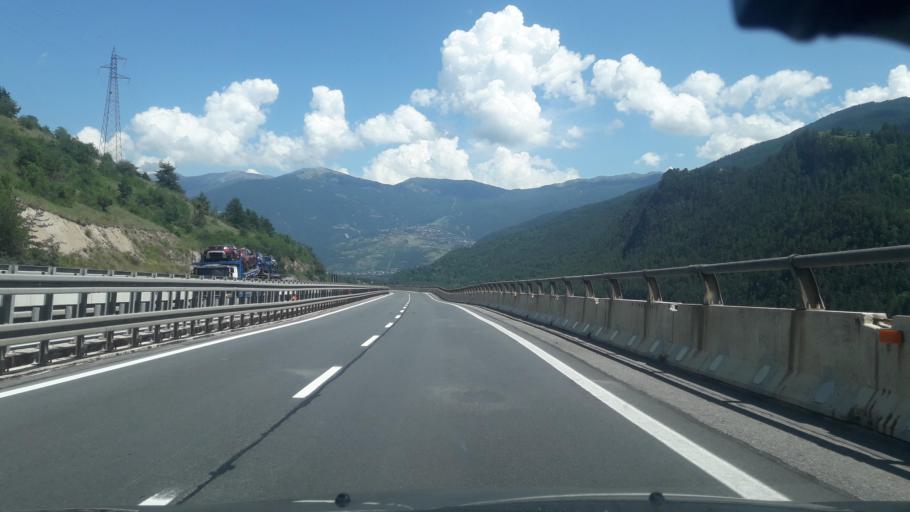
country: IT
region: Piedmont
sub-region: Provincia di Torino
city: Bardonecchia
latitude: 45.0470
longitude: 6.7618
